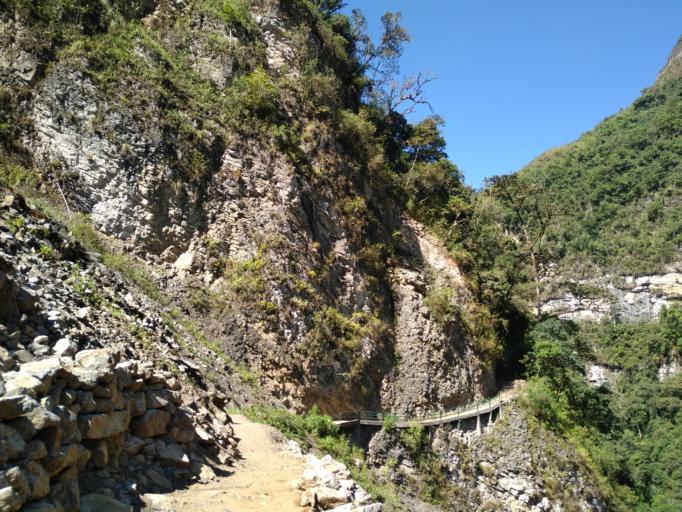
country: PE
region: Amazonas
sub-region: Provincia de Bongara
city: Churuja
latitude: -6.0348
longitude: -77.8893
